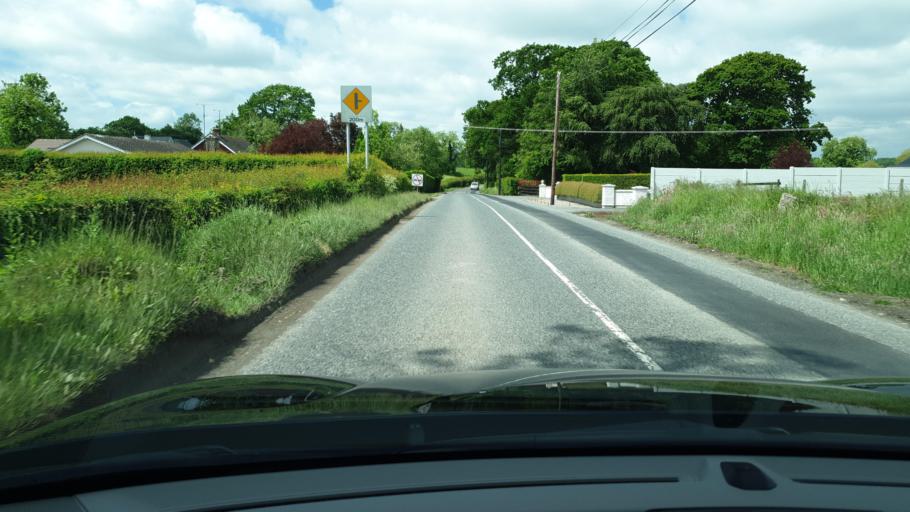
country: IE
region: Ulster
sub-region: An Cabhan
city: Kingscourt
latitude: 53.9006
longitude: -6.7765
